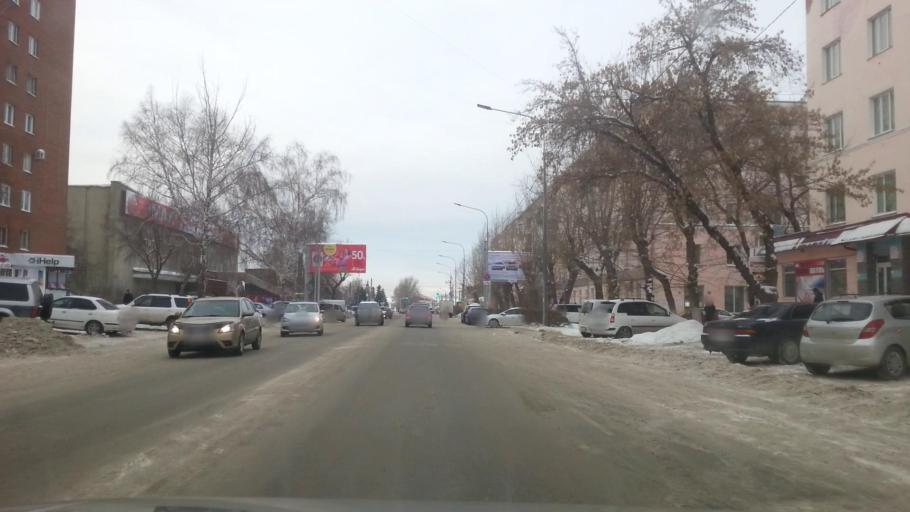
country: RU
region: Altai Krai
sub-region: Gorod Barnaulskiy
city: Barnaul
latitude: 53.3491
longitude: 83.7651
